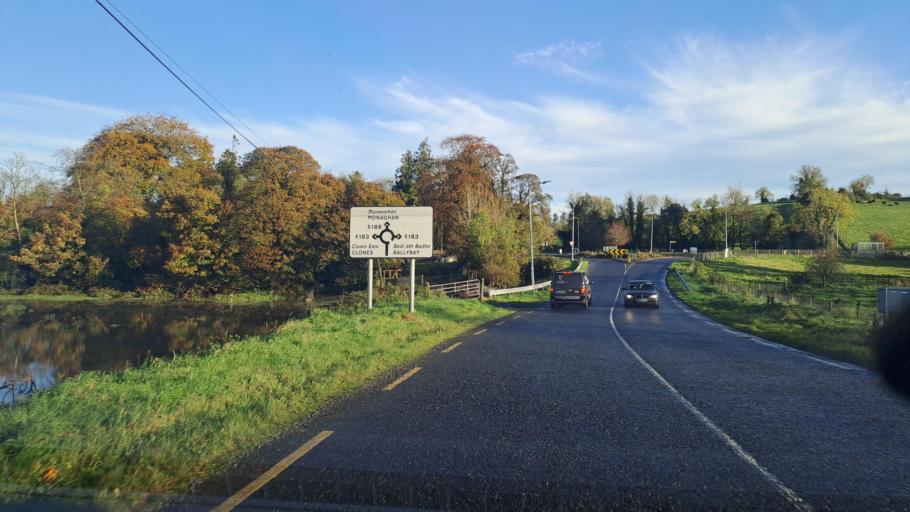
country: IE
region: Ulster
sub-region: An Cabhan
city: Cootehill
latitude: 54.1459
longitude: -7.0106
